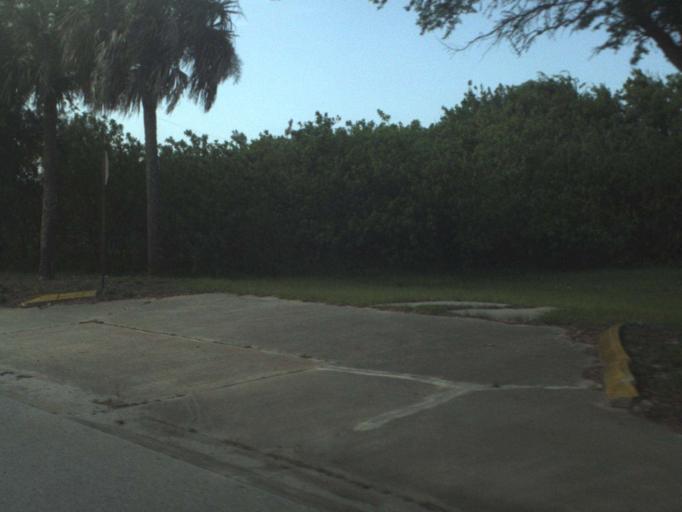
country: US
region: Florida
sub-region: Volusia County
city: South Daytona
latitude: 29.1610
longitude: -80.9963
